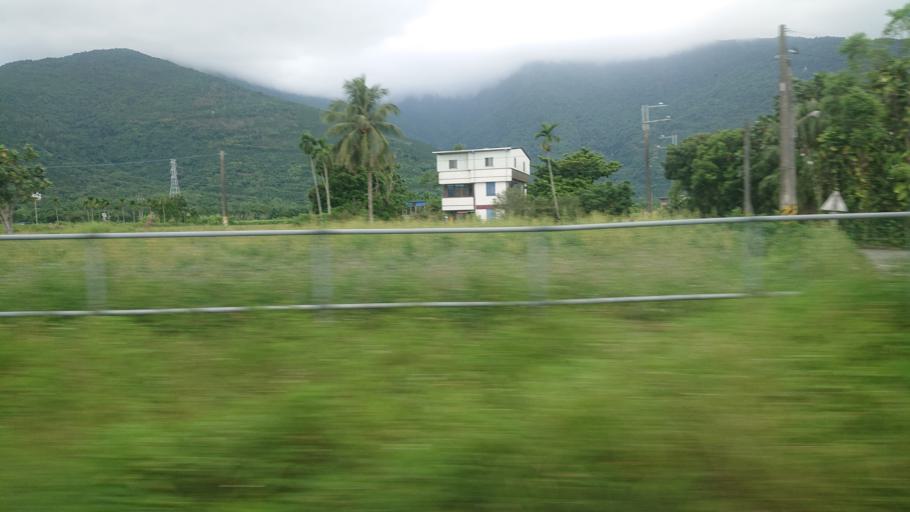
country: TW
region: Taiwan
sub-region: Hualien
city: Hualian
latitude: 23.7424
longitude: 121.4447
